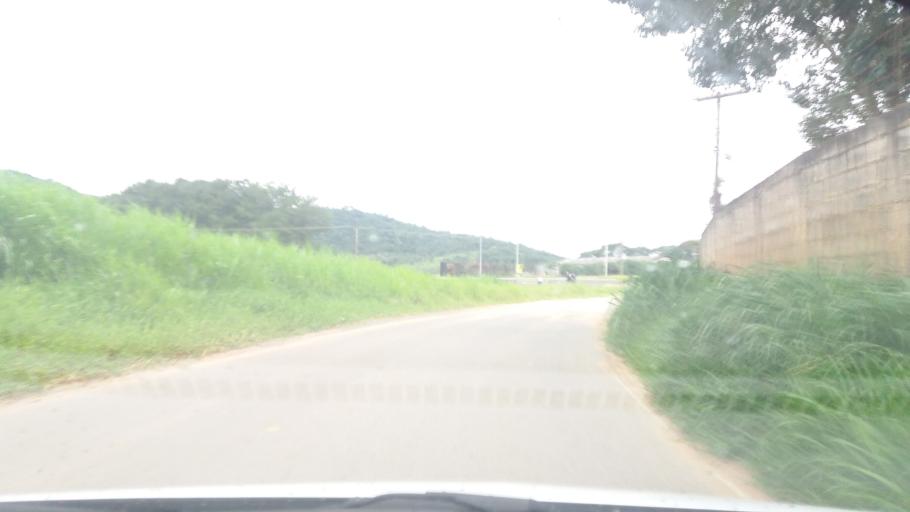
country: BR
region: Sao Paulo
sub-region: Bom Jesus Dos Perdoes
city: Bom Jesus dos Perdoes
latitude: -23.1633
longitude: -46.4473
